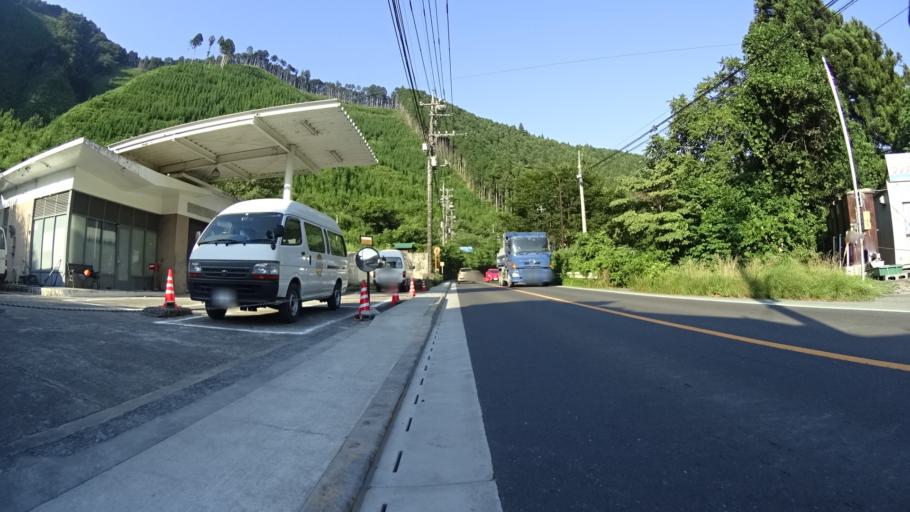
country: JP
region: Tokyo
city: Ome
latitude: 35.7991
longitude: 139.1790
